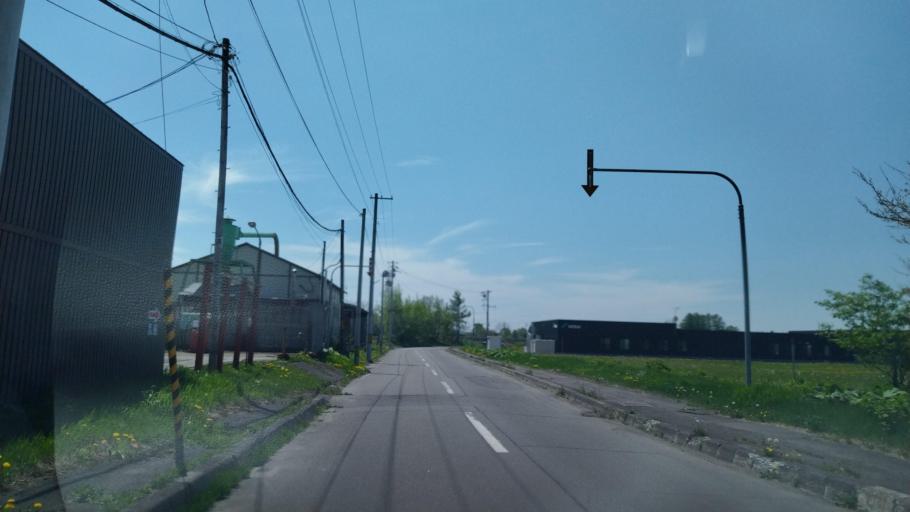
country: JP
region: Hokkaido
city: Otofuke
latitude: 43.2291
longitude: 143.2873
